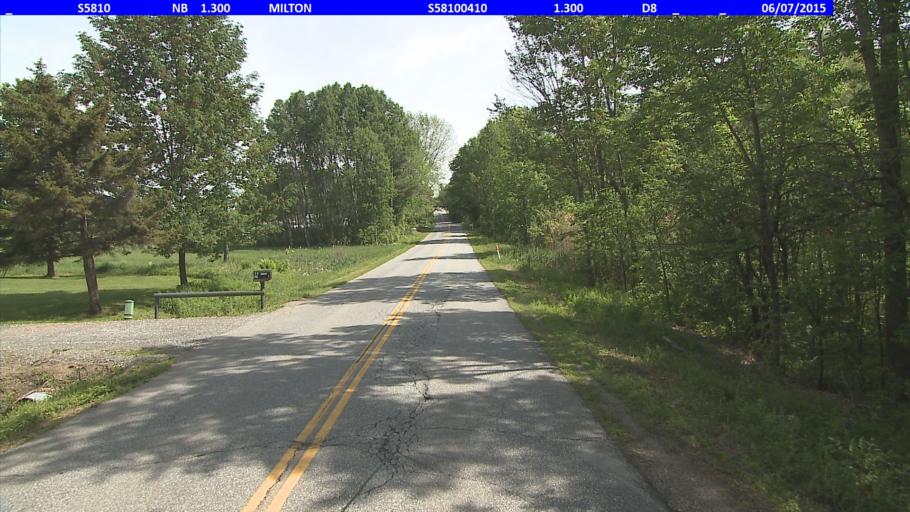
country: US
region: Vermont
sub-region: Chittenden County
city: Milton
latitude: 44.6001
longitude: -73.1278
